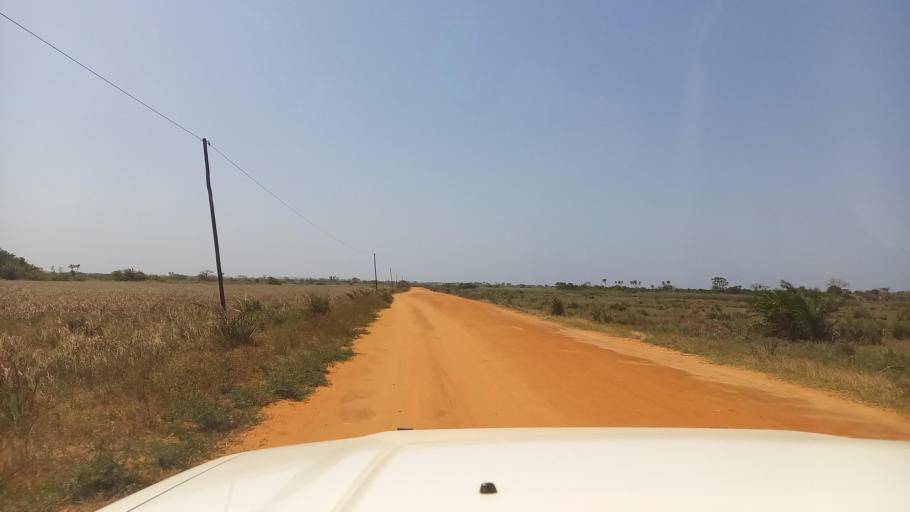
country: MZ
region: Cabo Delgado
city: Pemba
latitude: -13.4084
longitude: 40.5235
